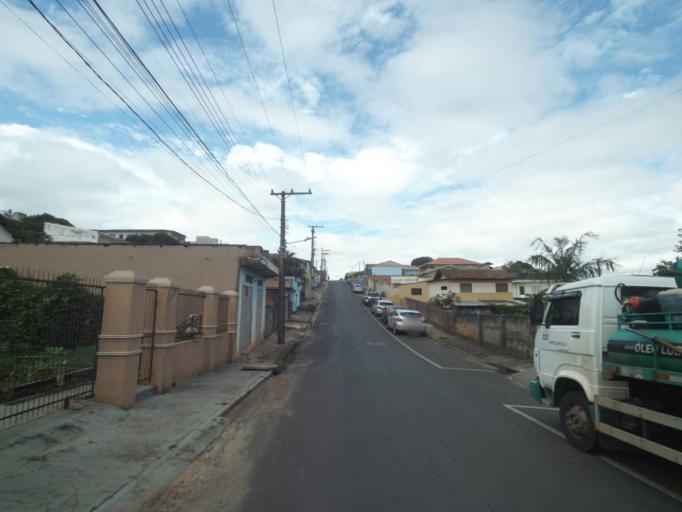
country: BR
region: Parana
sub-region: Telemaco Borba
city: Telemaco Borba
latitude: -24.3250
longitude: -50.6244
